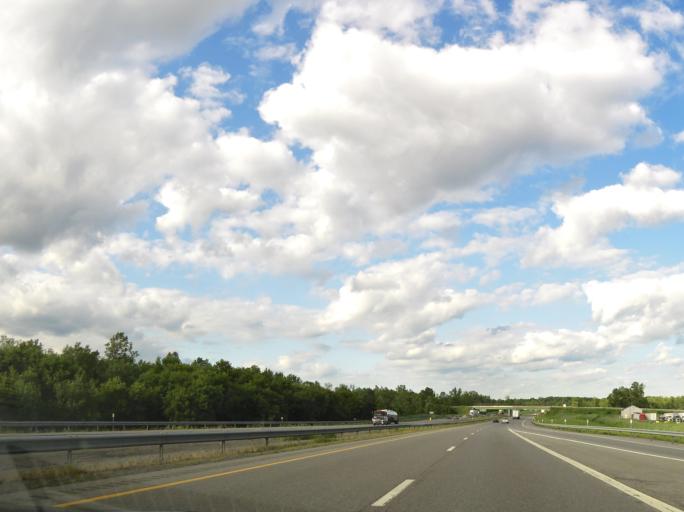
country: US
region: New York
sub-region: Erie County
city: Akron
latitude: 43.0050
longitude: -78.4097
